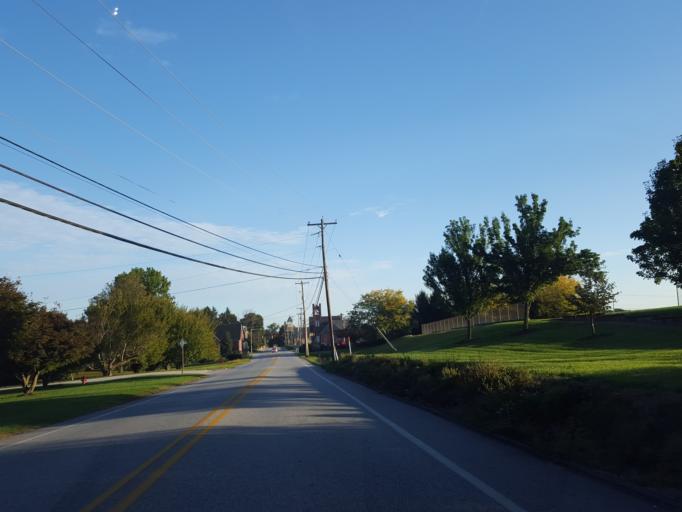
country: US
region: Pennsylvania
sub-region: York County
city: Windsor
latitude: 39.9257
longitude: -76.6066
